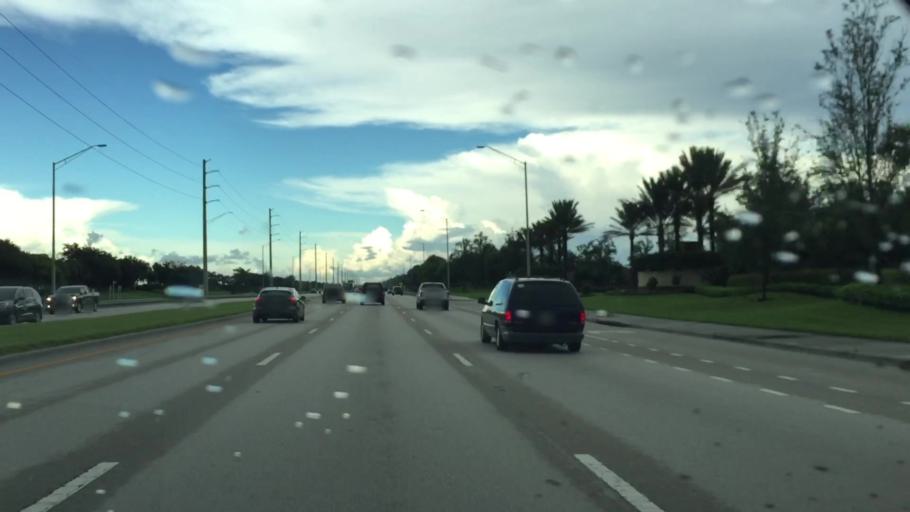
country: US
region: Florida
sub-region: Collier County
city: Vineyards
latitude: 26.2730
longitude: -81.6780
